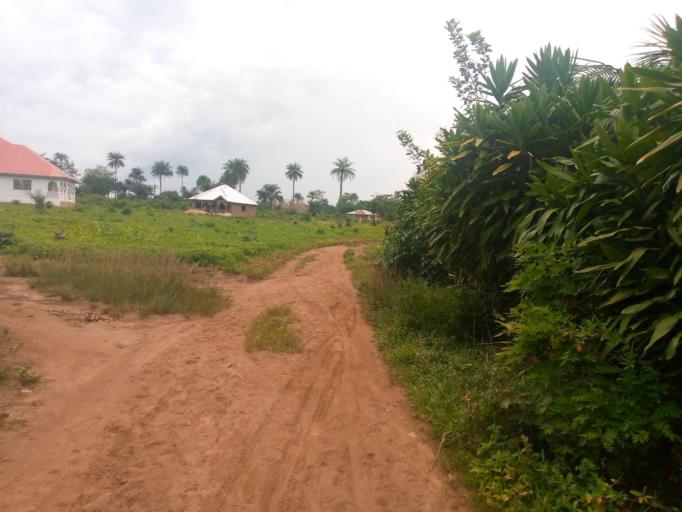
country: SL
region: Southern Province
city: Sumbuya
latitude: 7.6002
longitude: -12.1613
